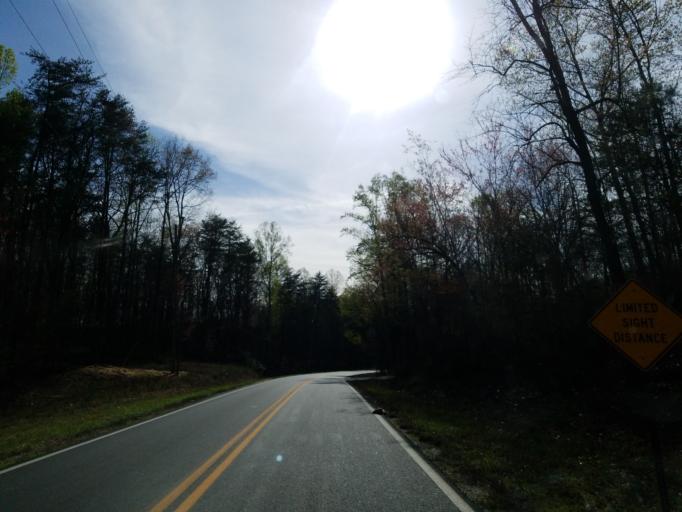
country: US
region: Georgia
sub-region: Dawson County
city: Dawsonville
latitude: 34.4718
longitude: -84.0585
